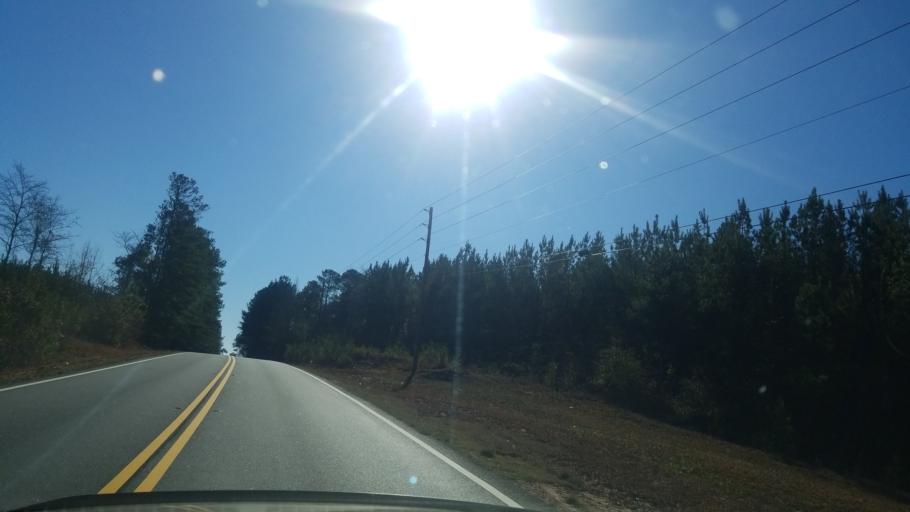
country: US
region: Alabama
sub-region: Chambers County
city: Valley
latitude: 32.8439
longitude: -85.1238
